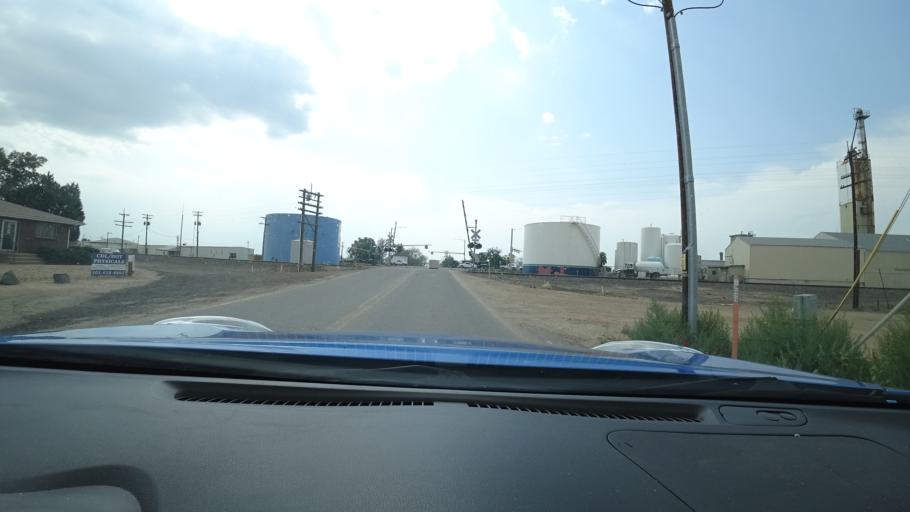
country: US
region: Colorado
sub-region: Adams County
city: Todd Creek
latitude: 39.9216
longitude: -104.8513
